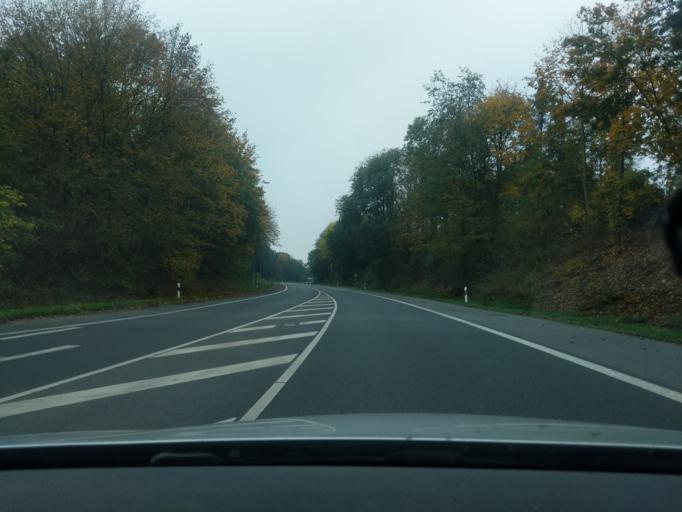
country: DE
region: Lower Saxony
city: Hemmoor
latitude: 53.6898
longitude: 9.1655
